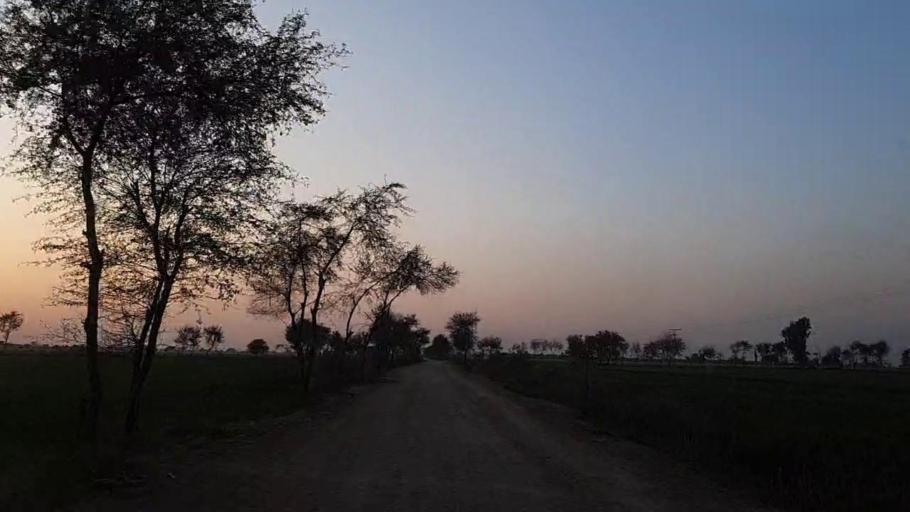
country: PK
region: Sindh
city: Bhit Shah
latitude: 25.9311
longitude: 68.4739
